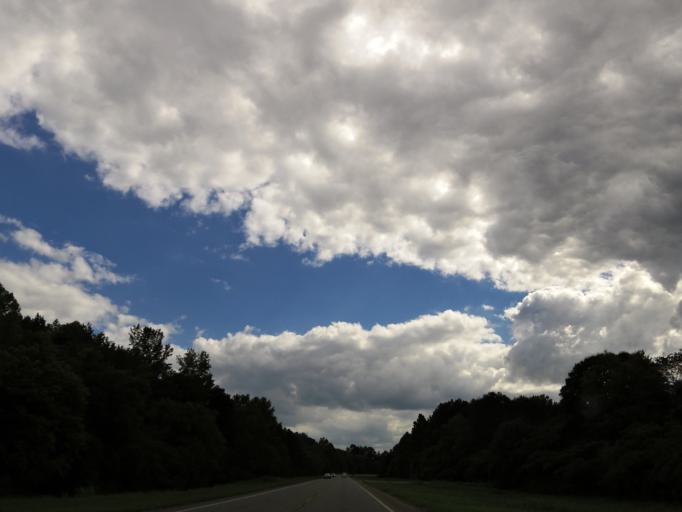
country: US
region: Georgia
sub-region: Walker County
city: Lookout Mountain
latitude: 34.9741
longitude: -85.3336
